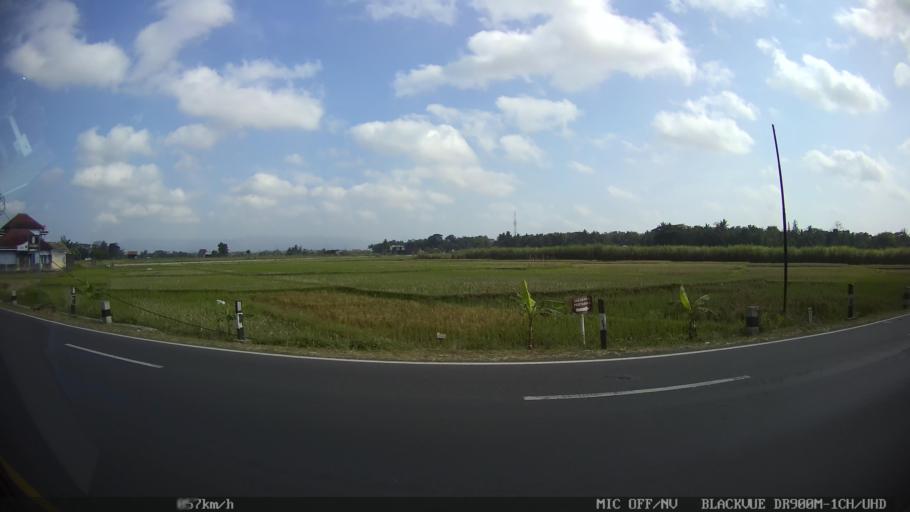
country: ID
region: Daerah Istimewa Yogyakarta
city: Godean
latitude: -7.8187
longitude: 110.2444
